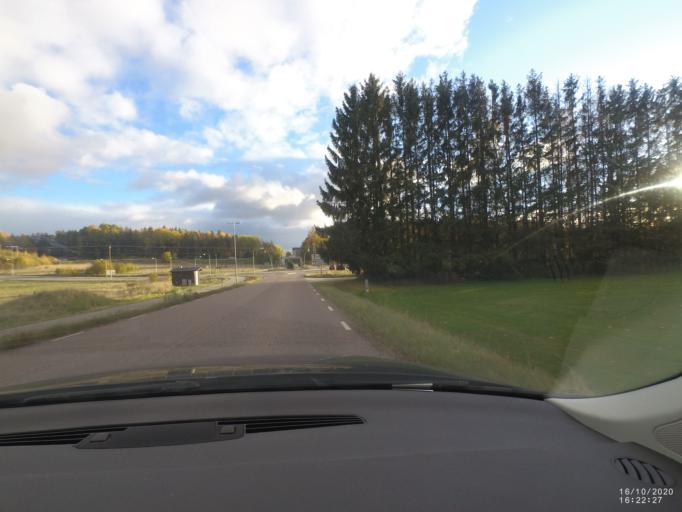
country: SE
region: Soedermanland
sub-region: Nykopings Kommun
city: Nykoping
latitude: 58.7718
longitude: 17.0067
